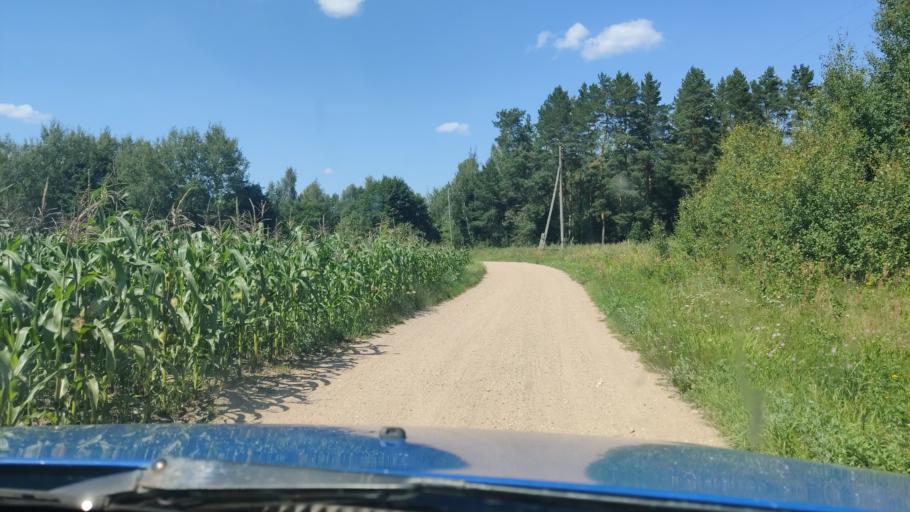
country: BY
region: Vitebsk
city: Byahoml'
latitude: 54.9703
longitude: 28.0249
